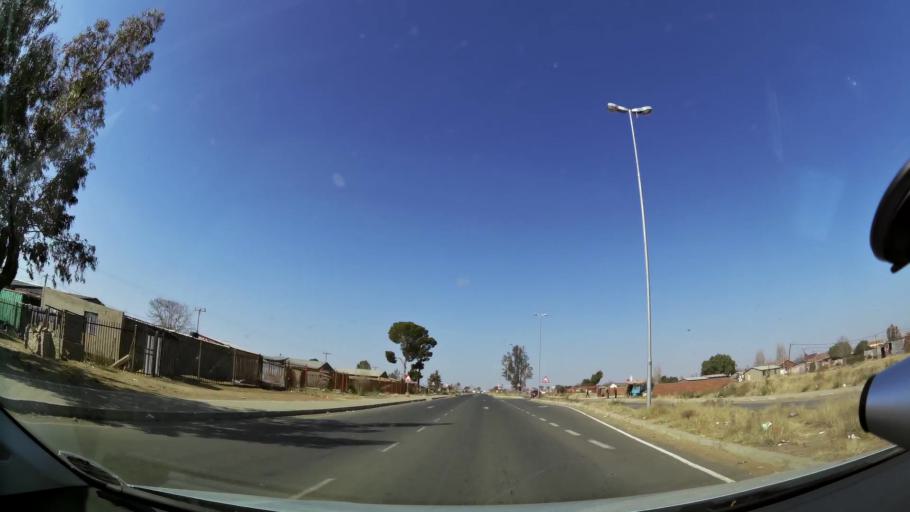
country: ZA
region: Orange Free State
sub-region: Mangaung Metropolitan Municipality
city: Bloemfontein
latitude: -29.1547
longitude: 26.2731
